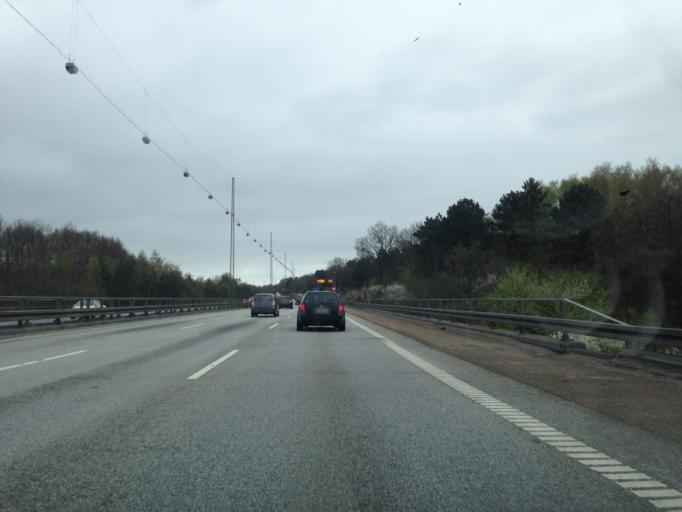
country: DK
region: Capital Region
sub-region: Rudersdal Kommune
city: Trorod
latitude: 55.8025
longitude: 12.5335
